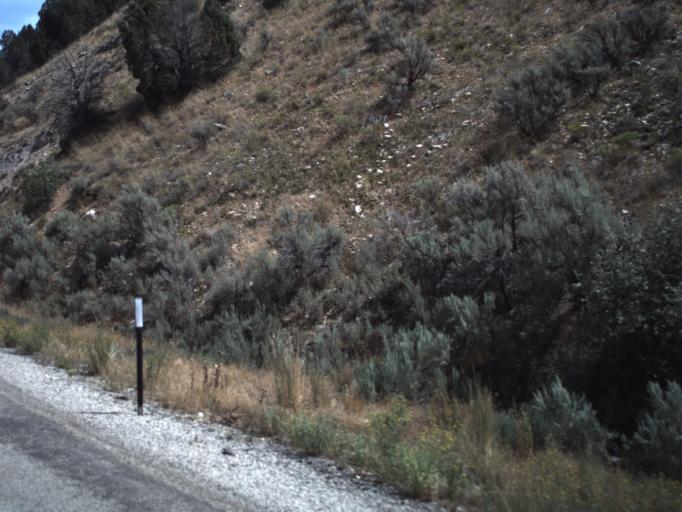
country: US
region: Utah
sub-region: Utah County
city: Woodland Hills
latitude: 39.9466
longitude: -111.5393
